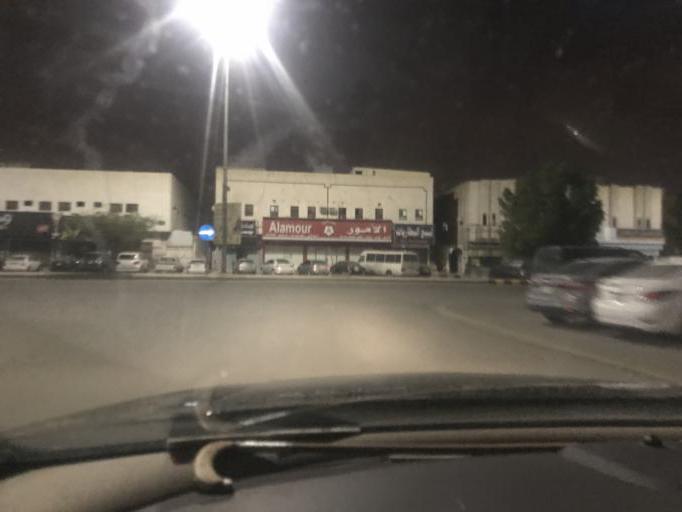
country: SA
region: Ar Riyad
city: Riyadh
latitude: 24.7334
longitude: 46.7758
